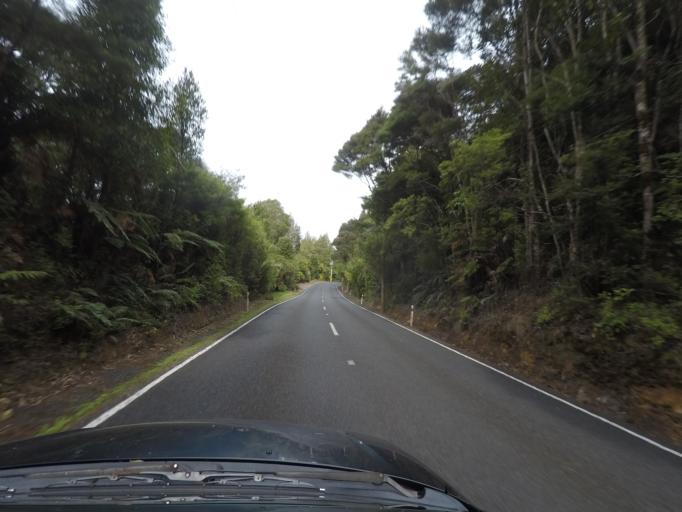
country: NZ
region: Auckland
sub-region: Auckland
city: Titirangi
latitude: -36.9403
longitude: 174.5825
